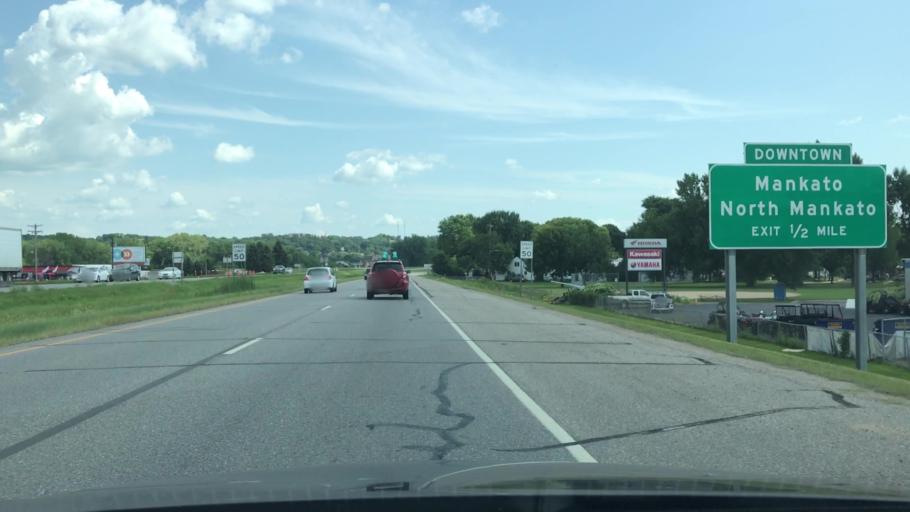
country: US
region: Minnesota
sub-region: Blue Earth County
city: Mankato
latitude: 44.1810
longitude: -94.0076
